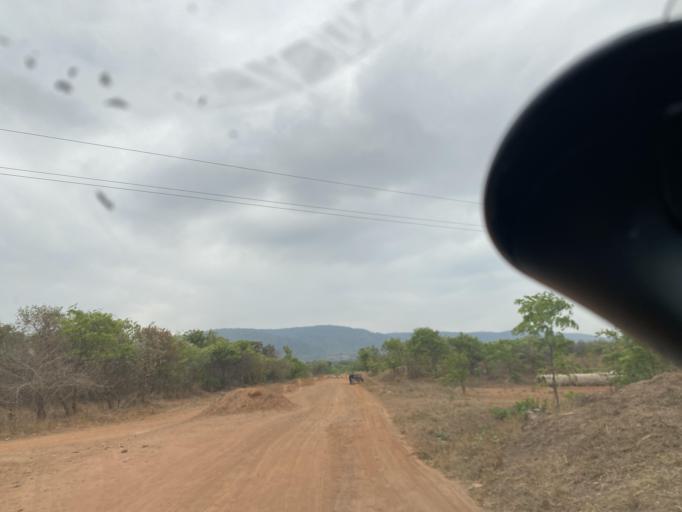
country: ZM
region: Lusaka
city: Chongwe
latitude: -15.2015
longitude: 28.7624
